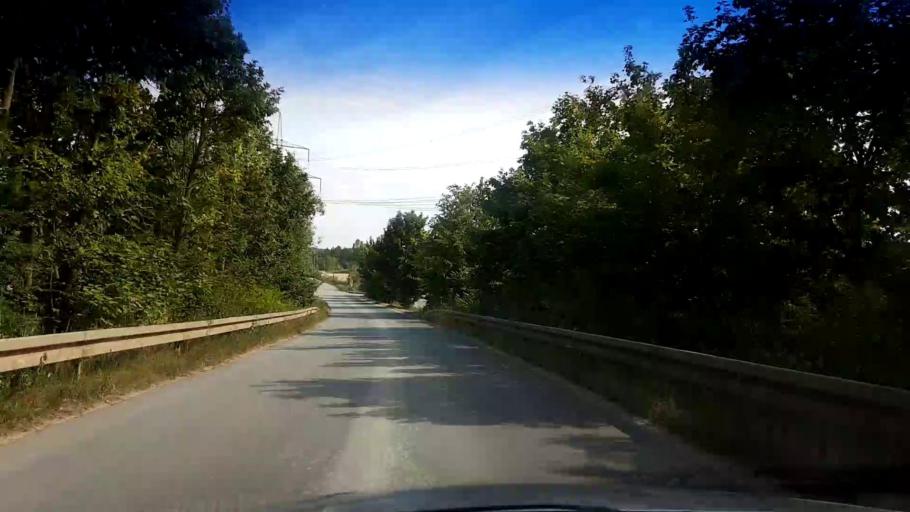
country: DE
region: Bavaria
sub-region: Regierungsbezirk Unterfranken
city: Stettfeld
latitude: 49.9652
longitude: 10.7210
